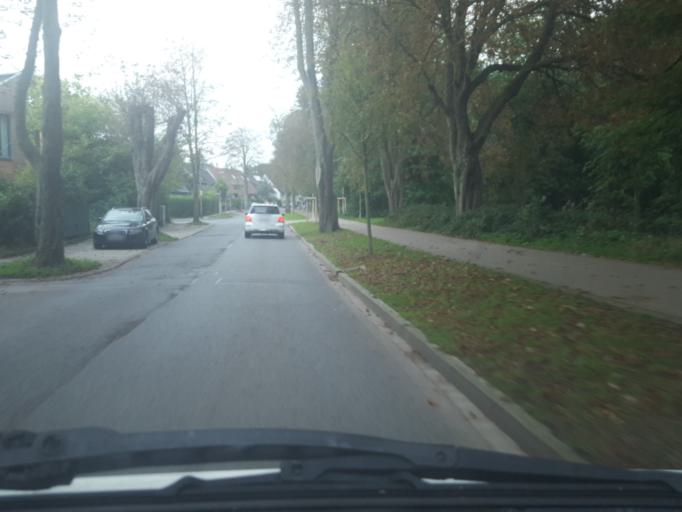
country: DE
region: North Rhine-Westphalia
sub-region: Regierungsbezirk Dusseldorf
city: Velbert
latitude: 51.3783
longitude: 7.0091
